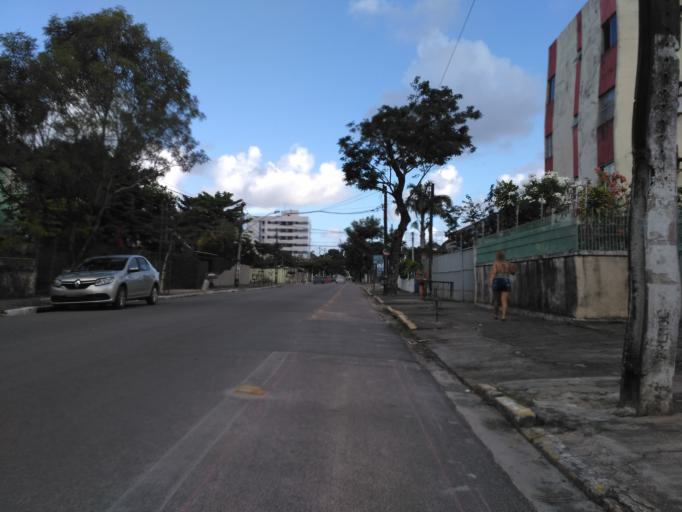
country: BR
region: Pernambuco
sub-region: Recife
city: Recife
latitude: -8.0500
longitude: -34.9410
